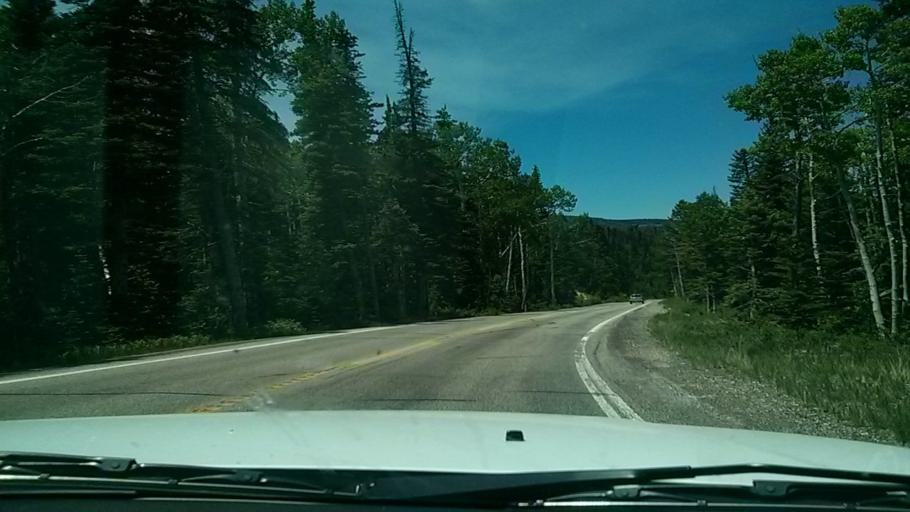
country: US
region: Utah
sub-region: Iron County
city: Cedar City
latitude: 37.5906
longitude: -112.8976
